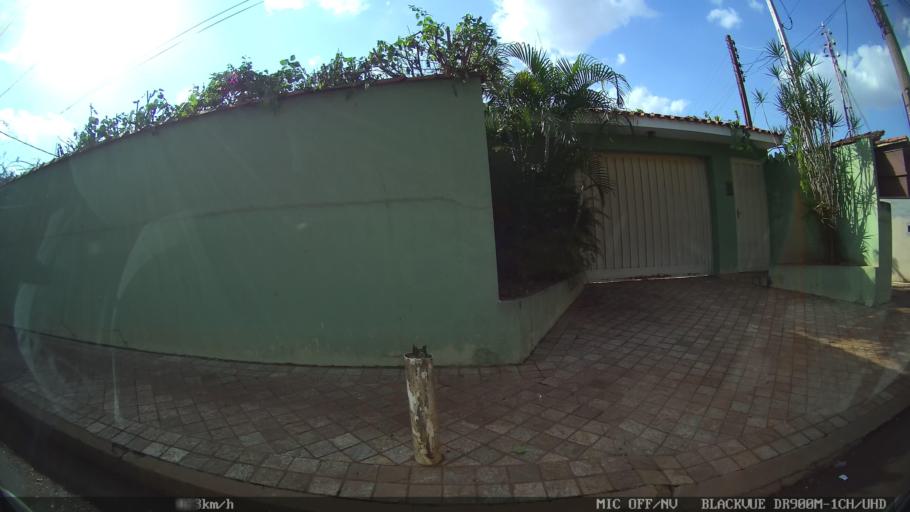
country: BR
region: Sao Paulo
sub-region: Ribeirao Preto
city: Ribeirao Preto
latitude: -21.1781
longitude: -47.8407
